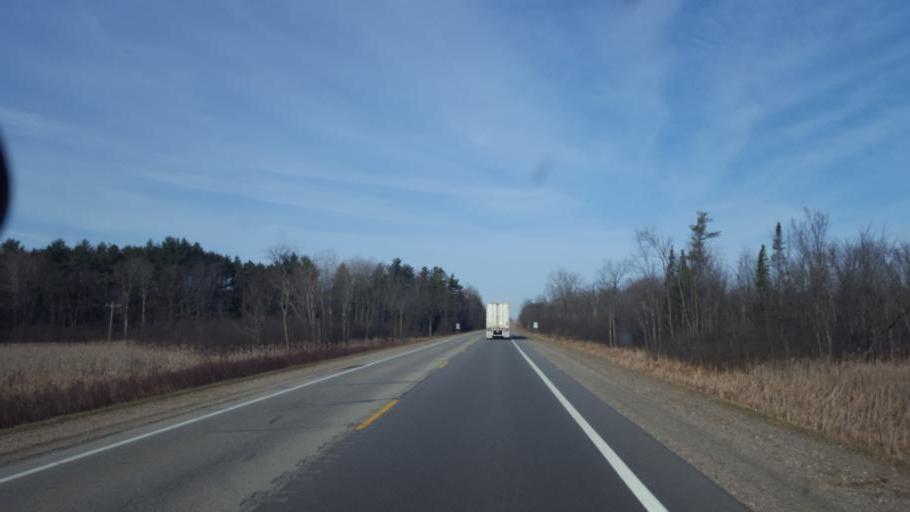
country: US
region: Michigan
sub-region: Montcalm County
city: Lakeview
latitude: 43.4309
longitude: -85.2209
